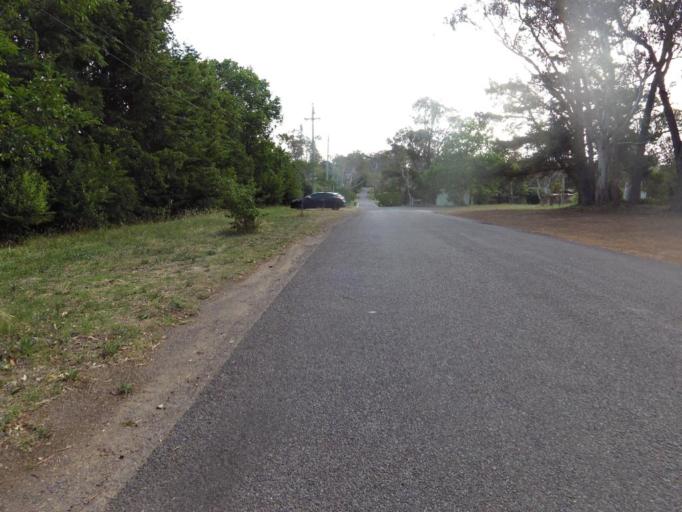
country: AU
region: Australian Capital Territory
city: Belconnen
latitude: -35.1691
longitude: 149.0699
